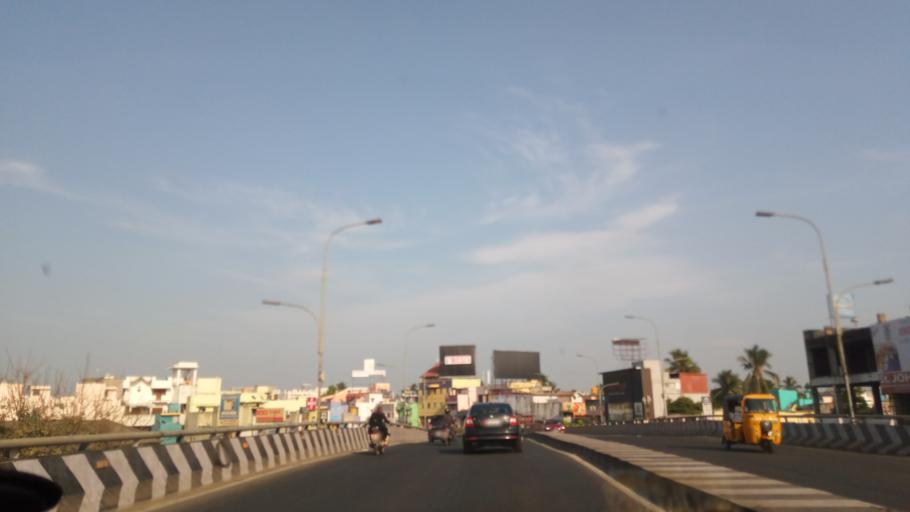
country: IN
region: Tamil Nadu
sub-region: Thiruvallur
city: Porur
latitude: 13.0348
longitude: 80.1560
